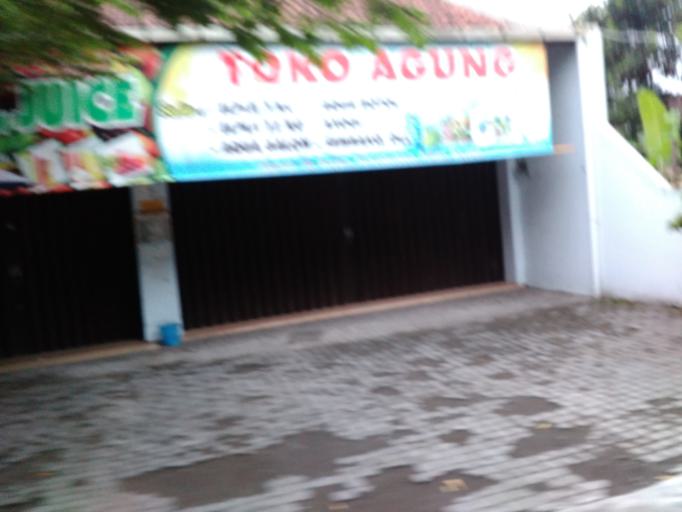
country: ID
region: Central Java
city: Boyolali
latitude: -7.5286
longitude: 110.5936
